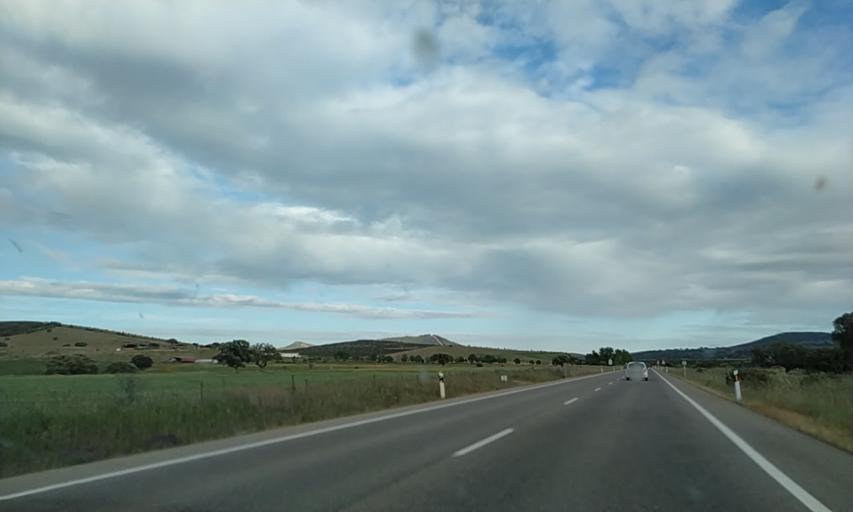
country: ES
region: Extremadura
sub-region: Provincia de Caceres
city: Pedroso de Acim
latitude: 39.8534
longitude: -6.4204
